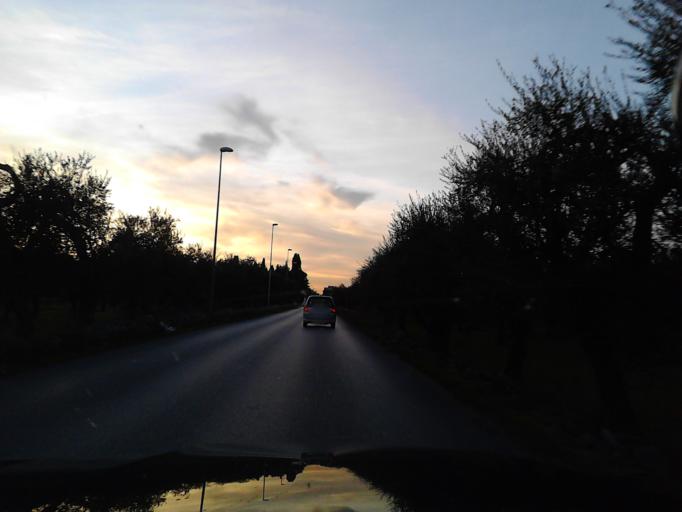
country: IT
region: Apulia
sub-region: Provincia di Bari
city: Valenzano
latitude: 41.0457
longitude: 16.8995
